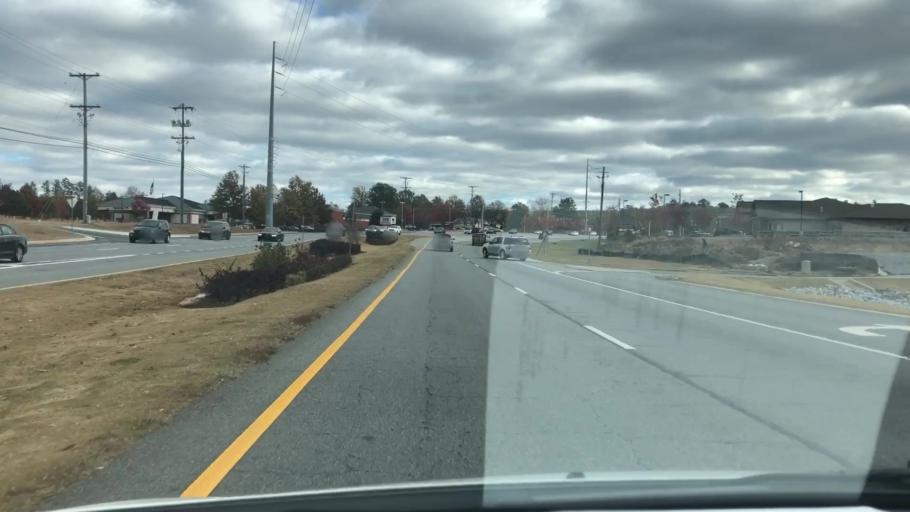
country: US
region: Georgia
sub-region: Fulton County
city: Johns Creek
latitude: 34.0865
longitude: -84.1642
